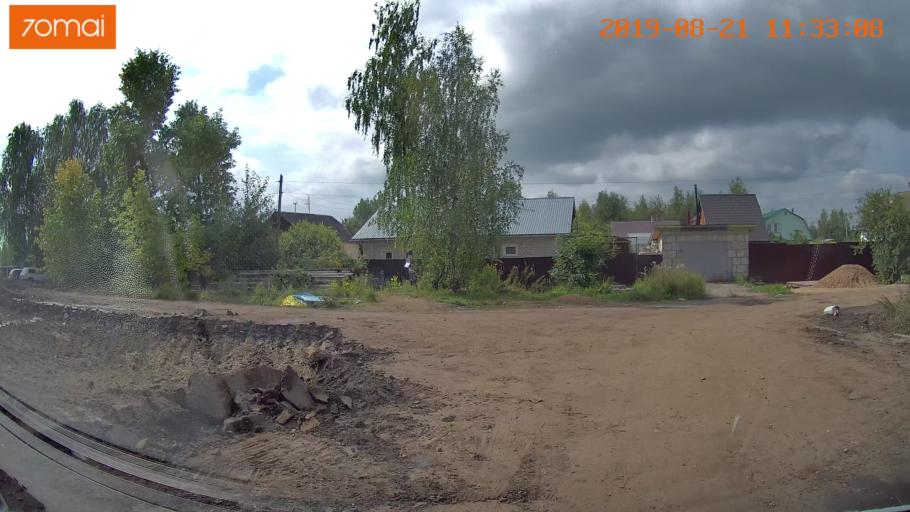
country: RU
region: Ivanovo
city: Novo-Talitsy
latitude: 56.9854
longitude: 40.9110
